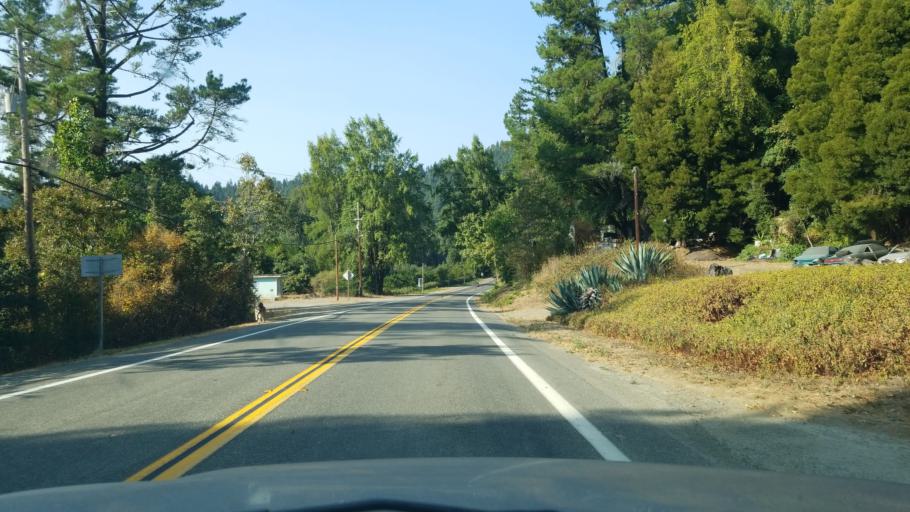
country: US
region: California
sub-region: Humboldt County
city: Redway
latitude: 40.2117
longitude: -123.7868
